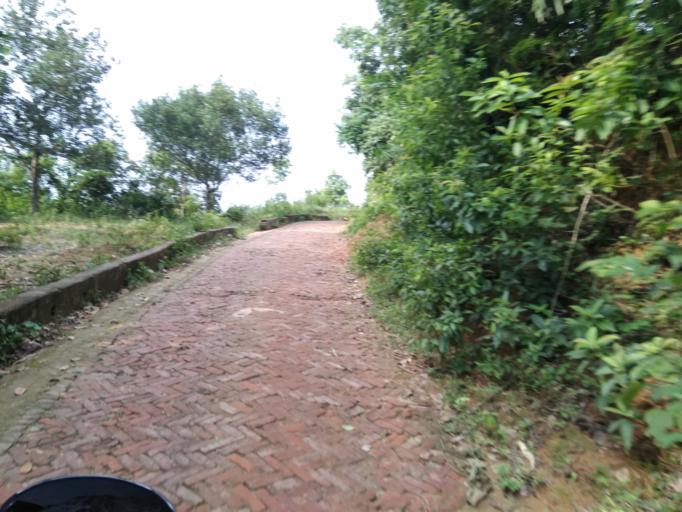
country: BD
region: Chittagong
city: Manikchari
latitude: 22.9267
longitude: 91.9124
